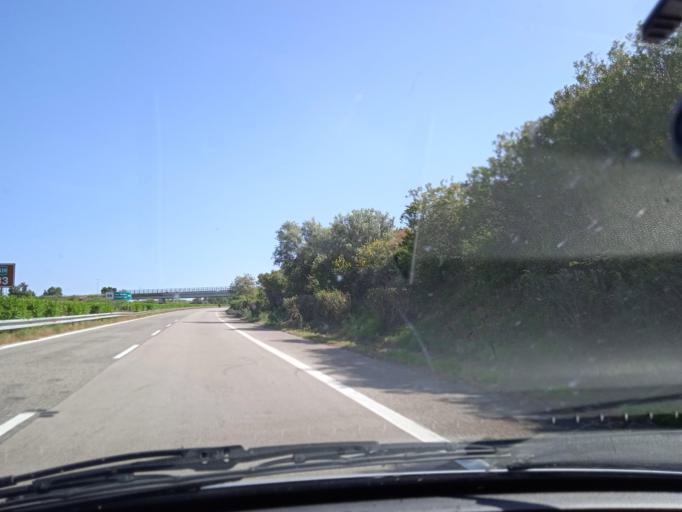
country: IT
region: Sicily
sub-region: Messina
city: Rocca di Capri Leone
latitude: 38.1190
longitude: 14.7268
